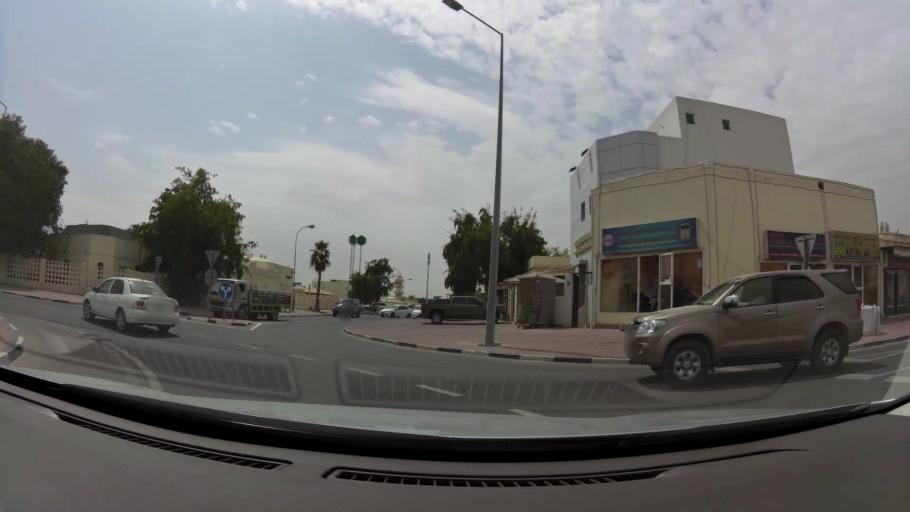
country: QA
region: Baladiyat ar Rayyan
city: Ar Rayyan
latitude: 25.3225
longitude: 51.4734
